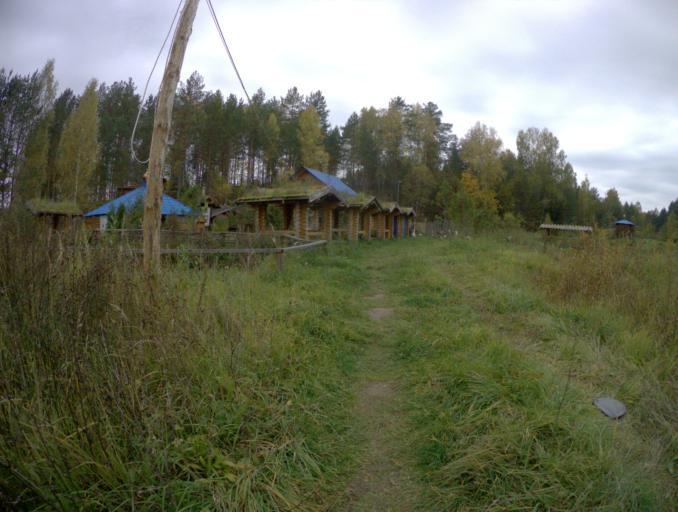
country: RU
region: Vladimir
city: Mstera
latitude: 56.3596
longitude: 41.8676
